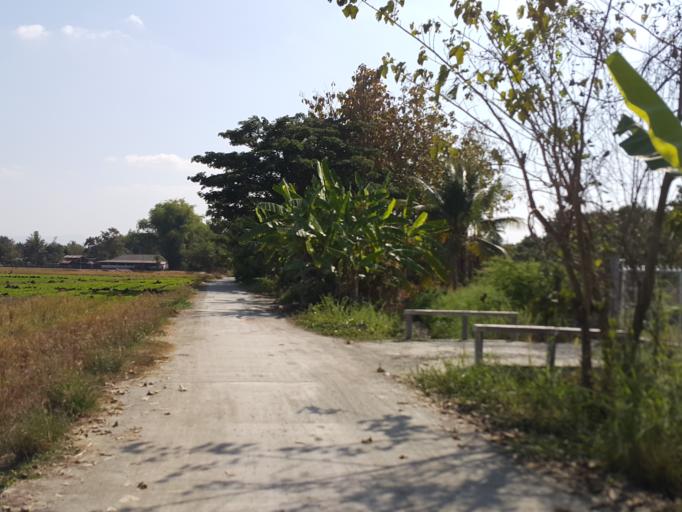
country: TH
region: Chiang Mai
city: San Kamphaeng
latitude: 18.8111
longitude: 99.1567
